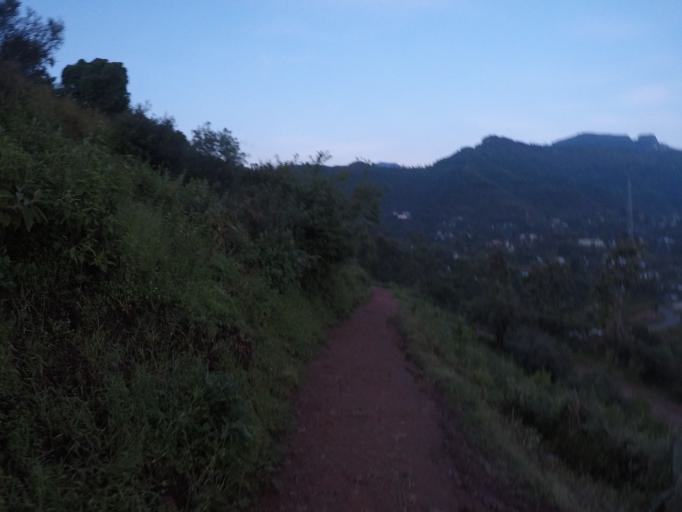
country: ET
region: Amhara
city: Lalibela
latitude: 12.0307
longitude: 39.0452
